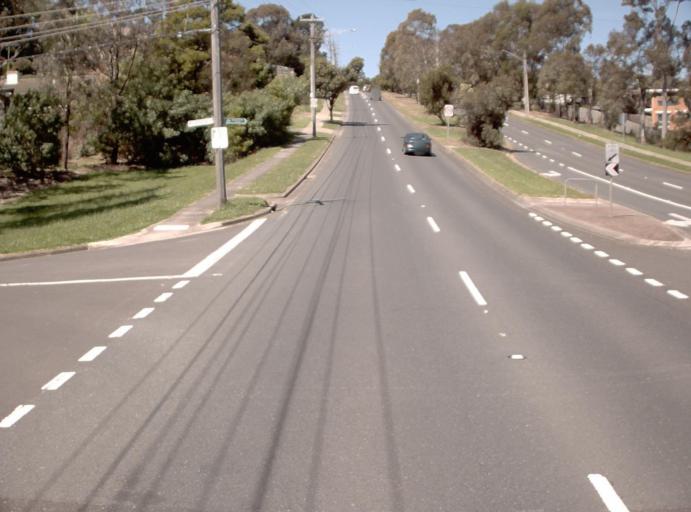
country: AU
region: Victoria
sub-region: Manningham
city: Templestowe Lower
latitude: -37.7585
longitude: 145.1247
